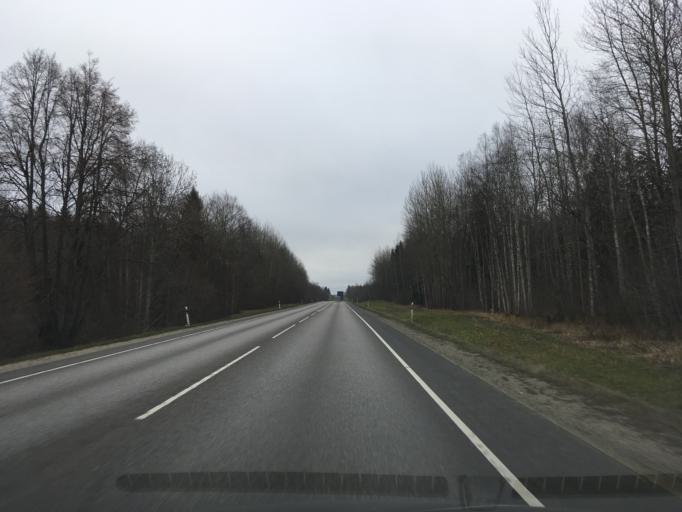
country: EE
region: Ida-Virumaa
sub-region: Sillamaee linn
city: Sillamae
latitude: 59.3811
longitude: 27.8550
